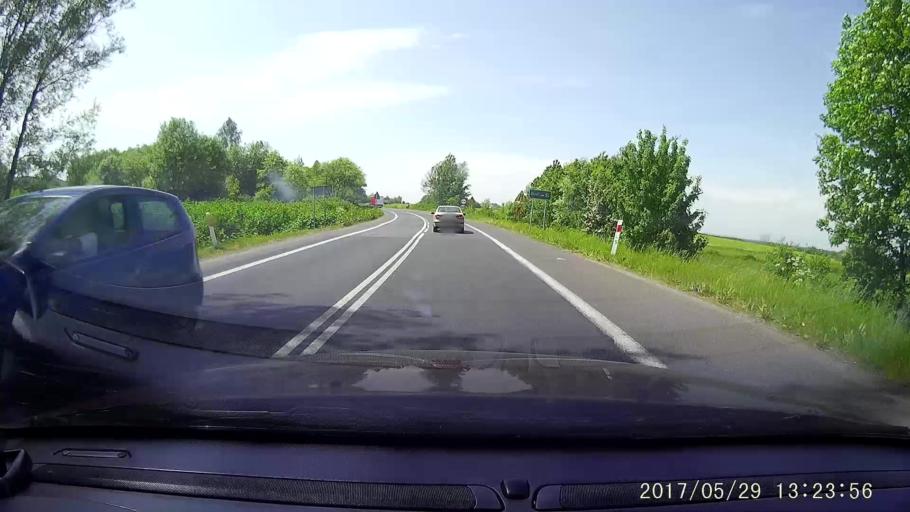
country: PL
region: Lower Silesian Voivodeship
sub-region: Powiat lwowecki
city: Gryfow Slaski
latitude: 51.0356
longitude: 15.4025
